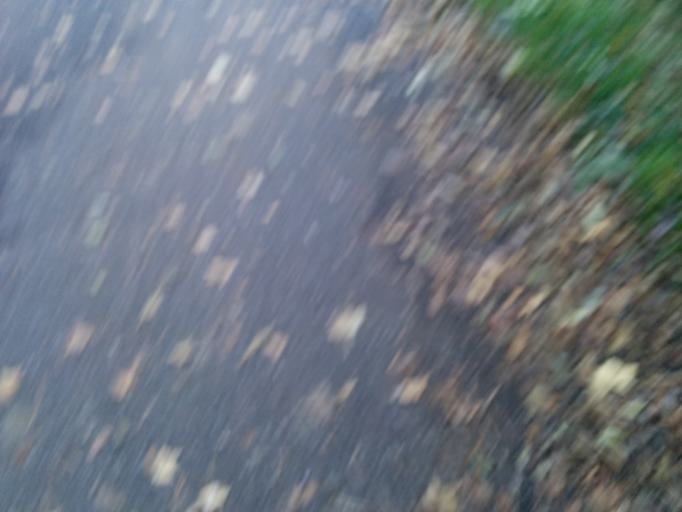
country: DE
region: North Rhine-Westphalia
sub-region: Regierungsbezirk Dusseldorf
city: Heiligenhaus
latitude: 51.3748
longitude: 6.9628
